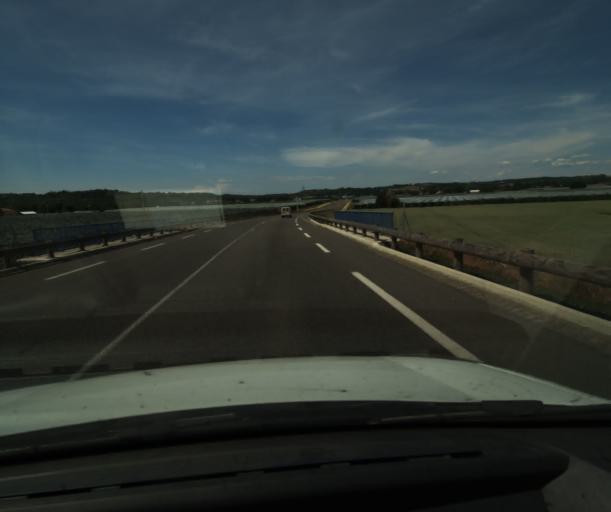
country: FR
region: Midi-Pyrenees
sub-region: Departement du Tarn-et-Garonne
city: Moissac
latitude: 44.0928
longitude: 1.1128
